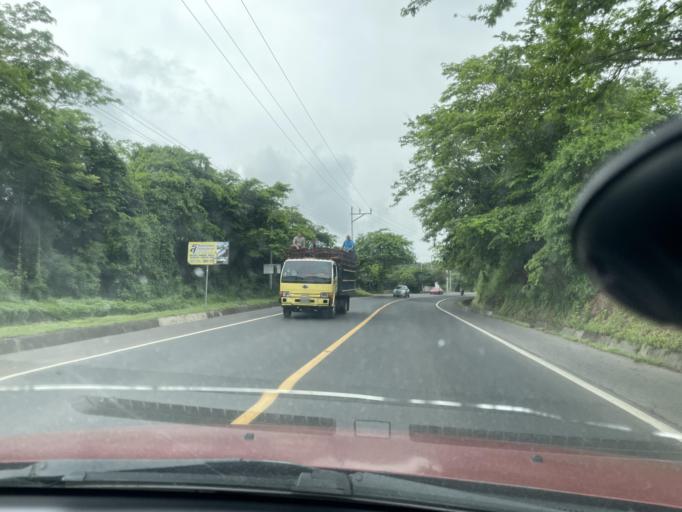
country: SV
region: San Miguel
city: San Miguel
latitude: 13.5218
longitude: -88.1445
